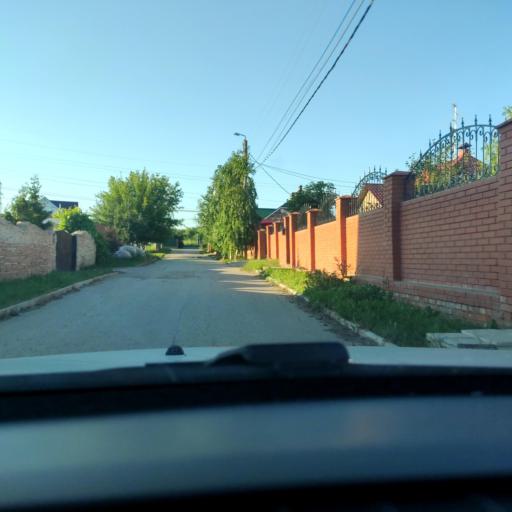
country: RU
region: Samara
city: Kinel'
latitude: 53.2751
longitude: 50.5909
